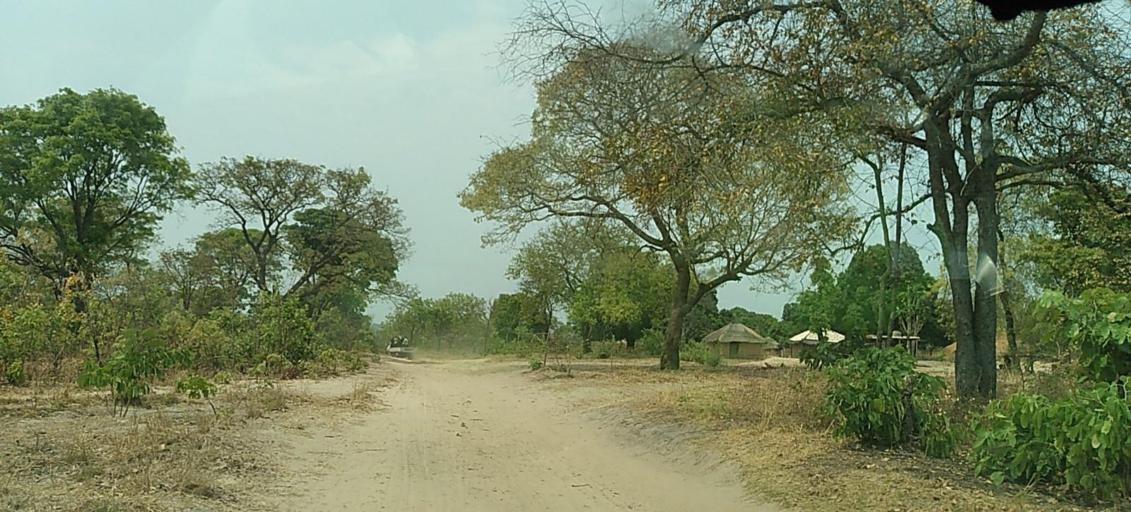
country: ZM
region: North-Western
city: Kabompo
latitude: -13.4786
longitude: 24.4576
